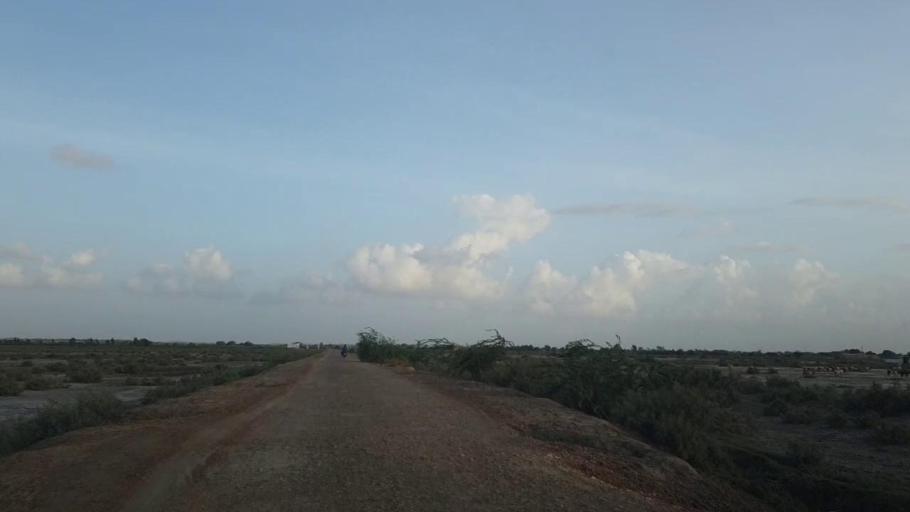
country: PK
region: Sindh
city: Kadhan
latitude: 24.5538
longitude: 69.1233
